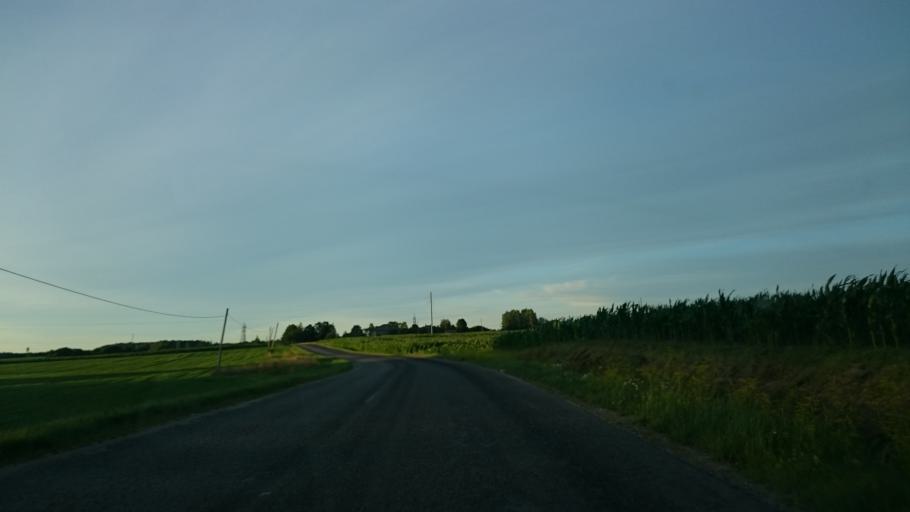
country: LV
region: Saldus Rajons
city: Saldus
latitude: 56.6828
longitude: 22.5020
